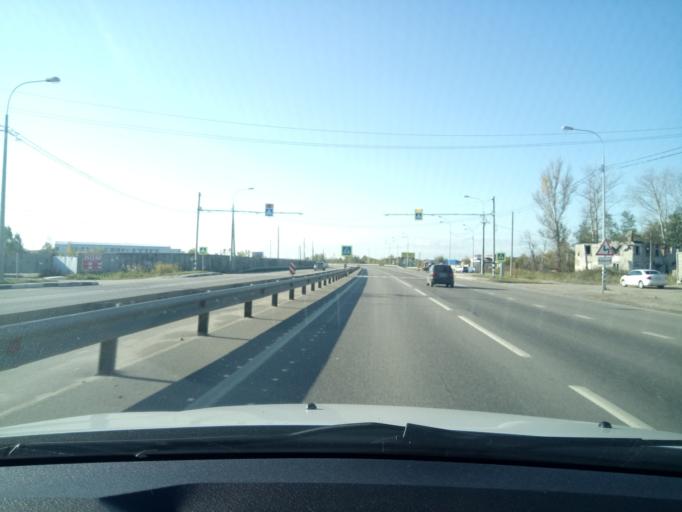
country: RU
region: Nizjnij Novgorod
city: Burevestnik
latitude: 56.1614
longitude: 43.9137
